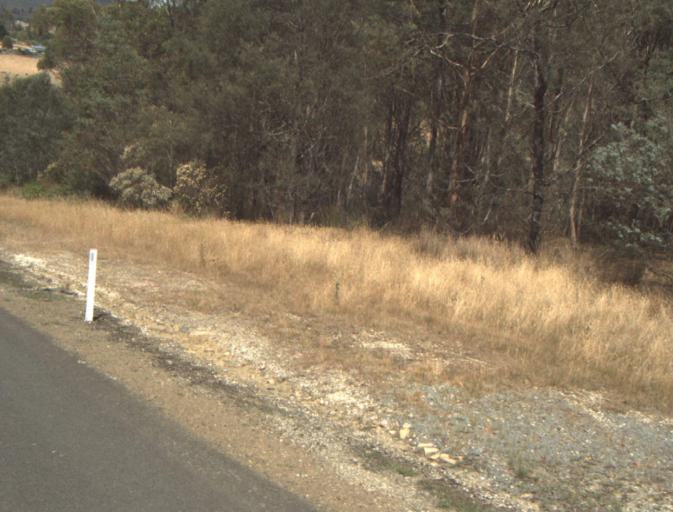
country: AU
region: Tasmania
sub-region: Launceston
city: Mayfield
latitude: -41.2182
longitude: 147.1373
